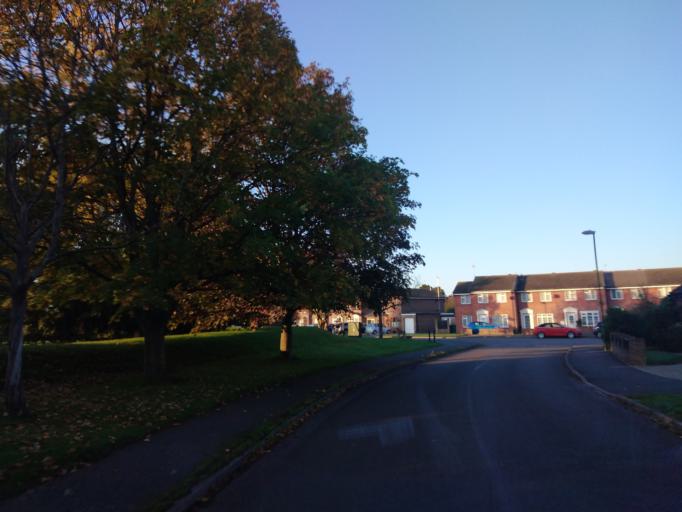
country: GB
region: England
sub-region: West Sussex
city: Rustington
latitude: 50.8150
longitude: -0.5207
